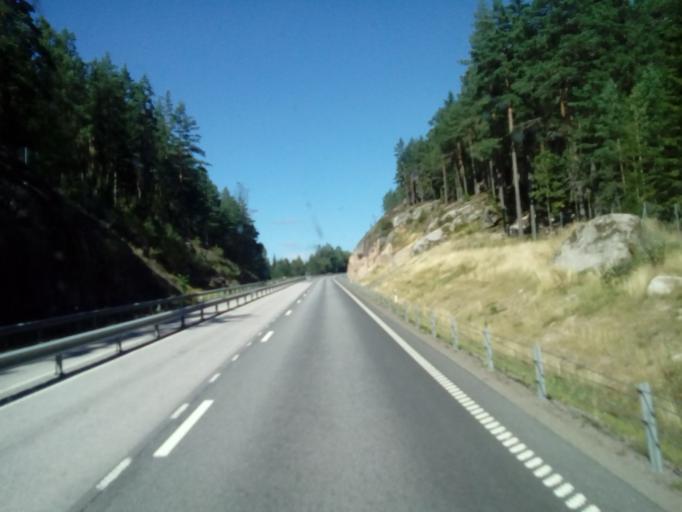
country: SE
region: OEstergoetland
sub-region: Kinda Kommun
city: Rimforsa
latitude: 58.0807
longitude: 15.6509
